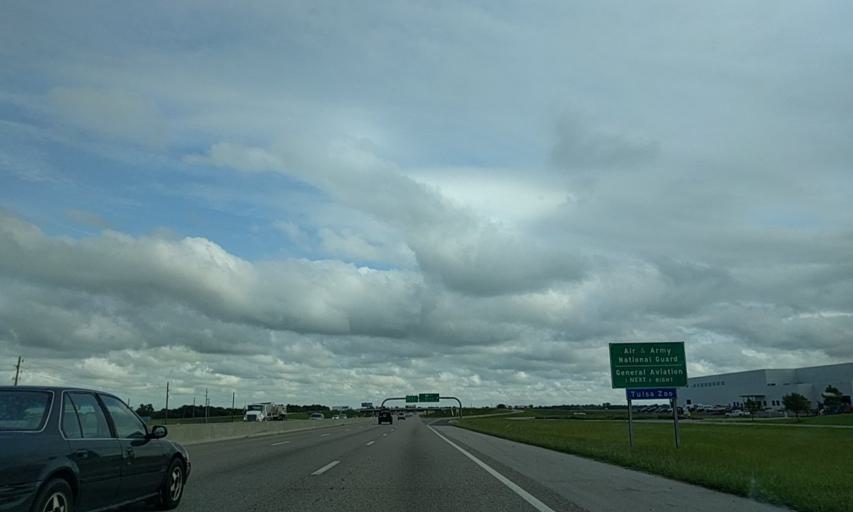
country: US
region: Oklahoma
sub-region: Tulsa County
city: Owasso
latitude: 36.2151
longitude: -95.8516
